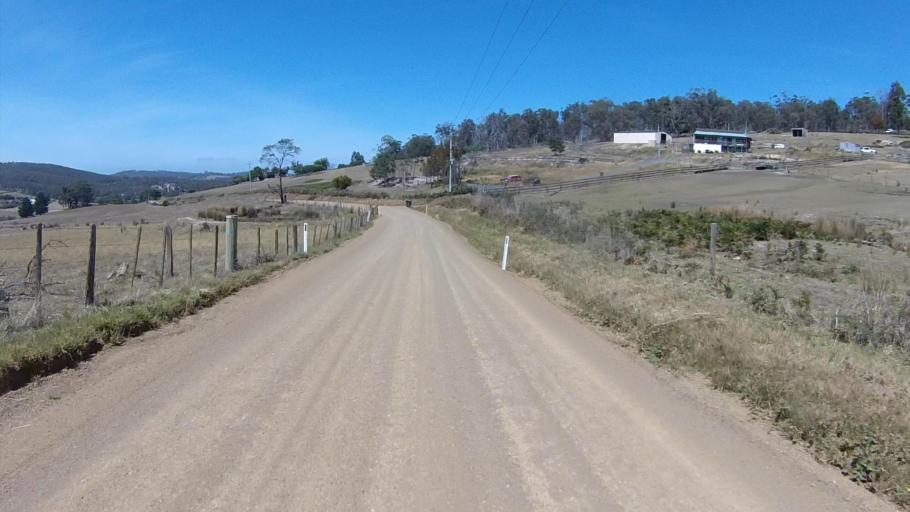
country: AU
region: Tasmania
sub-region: Sorell
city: Sorell
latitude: -42.7903
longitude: 147.6379
